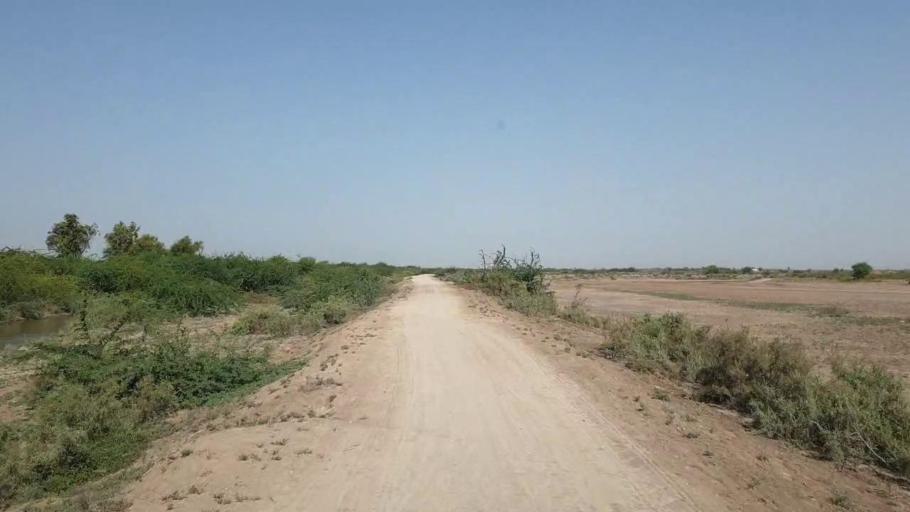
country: PK
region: Sindh
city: Tando Bago
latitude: 24.6501
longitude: 69.0711
